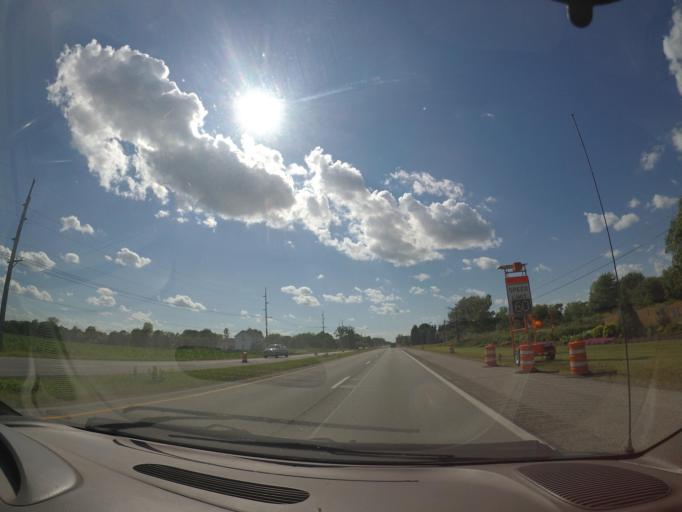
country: US
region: Ohio
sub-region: Sandusky County
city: Clyde
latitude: 41.3287
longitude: -83.0432
